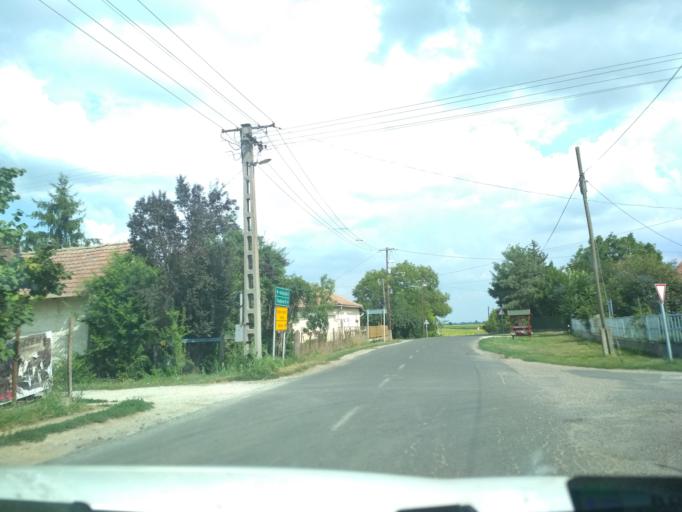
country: HU
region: Jasz-Nagykun-Szolnok
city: Abadszalok
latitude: 47.5118
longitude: 20.6485
